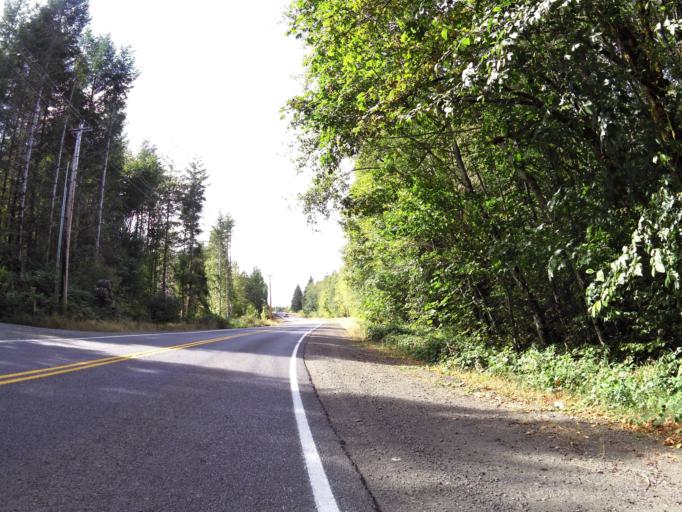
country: US
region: Washington
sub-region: Mason County
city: Shelton
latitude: 47.1497
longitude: -123.0643
